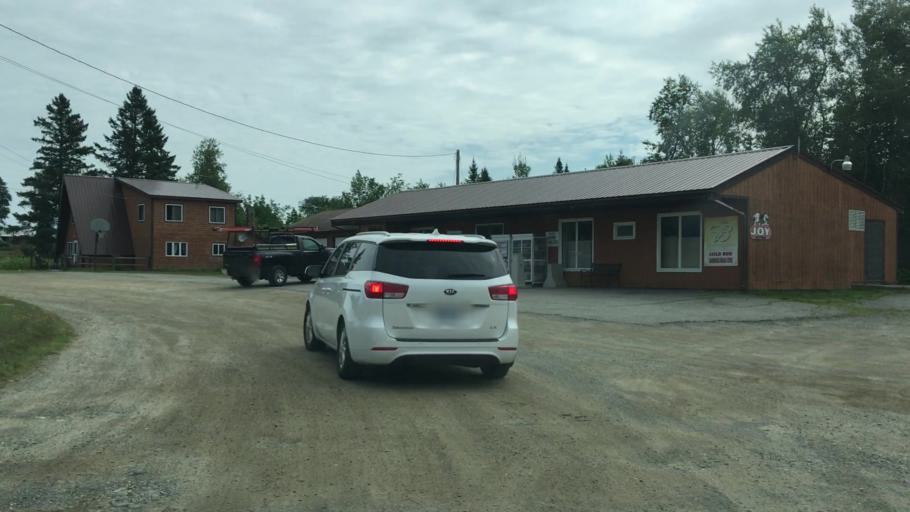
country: US
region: Maine
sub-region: Washington County
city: Calais
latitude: 45.0941
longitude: -67.4684
